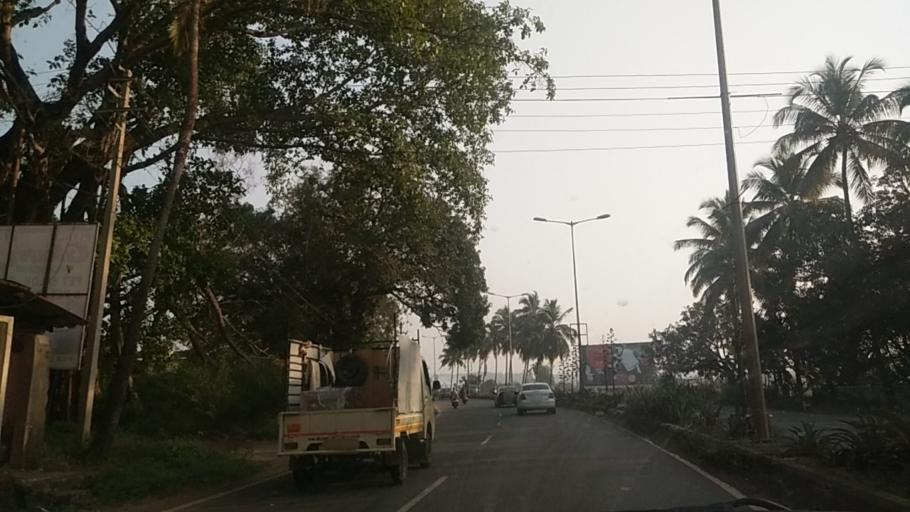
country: IN
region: Goa
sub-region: North Goa
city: Guirim
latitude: 15.5672
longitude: 73.8075
